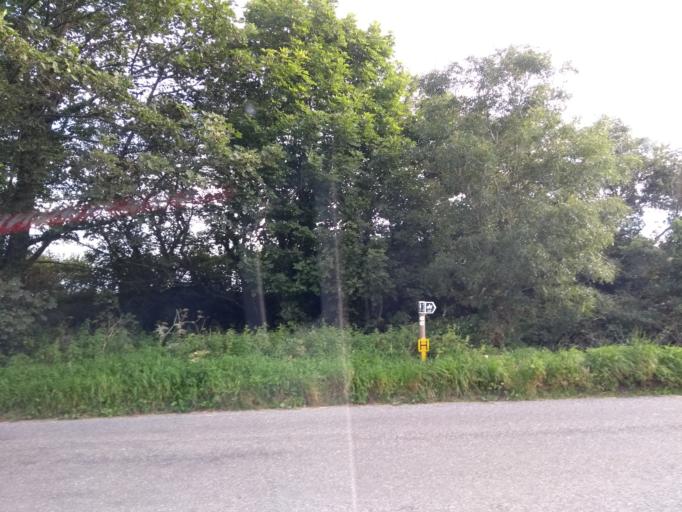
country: GB
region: England
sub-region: Dorset
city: Beaminster
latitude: 50.8280
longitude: -2.7241
